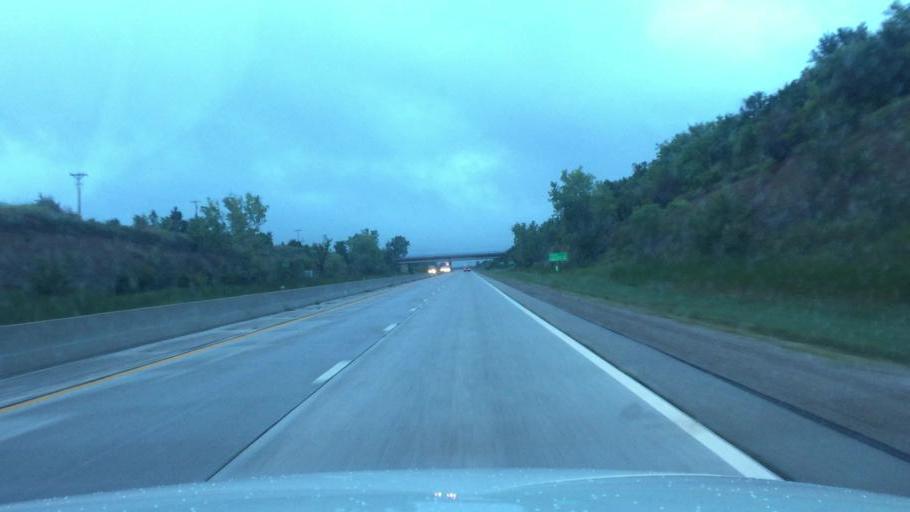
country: US
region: Kansas
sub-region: Neosho County
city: Chanute
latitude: 37.6786
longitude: -95.4796
